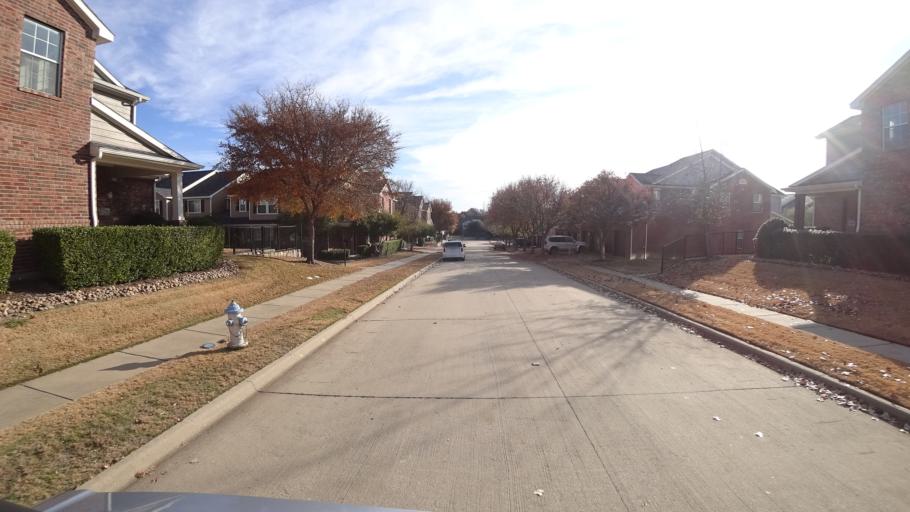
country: US
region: Texas
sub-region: Collin County
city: McKinney
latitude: 33.2053
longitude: -96.6421
